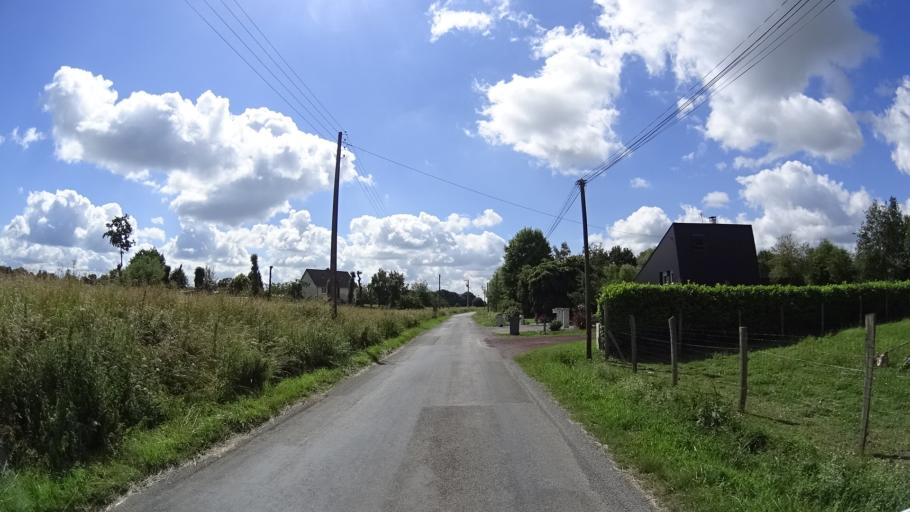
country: FR
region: Brittany
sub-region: Departement d'Ille-et-Vilaine
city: Le Rheu
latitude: 48.1158
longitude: -1.8164
